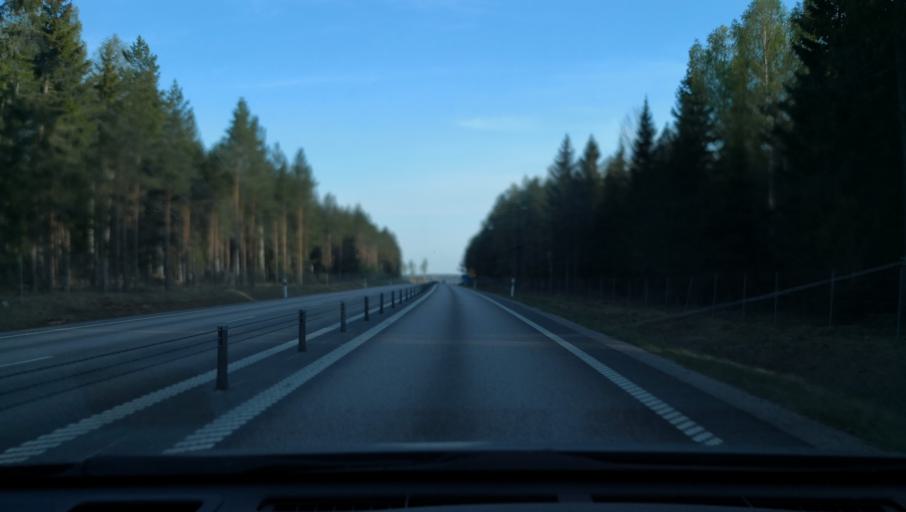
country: SE
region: Uppsala
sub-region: Heby Kommun
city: Heby
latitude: 59.9636
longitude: 16.8359
